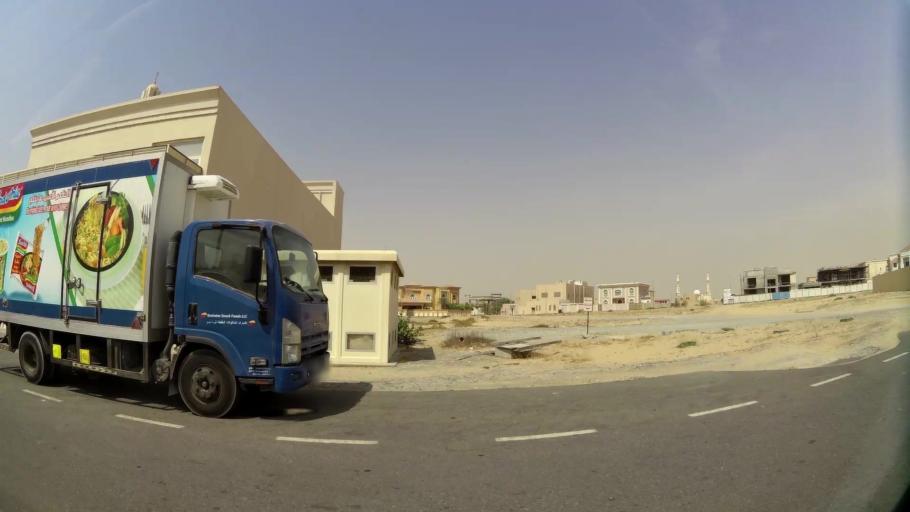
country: AE
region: Ash Shariqah
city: Sharjah
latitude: 25.2446
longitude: 55.4975
